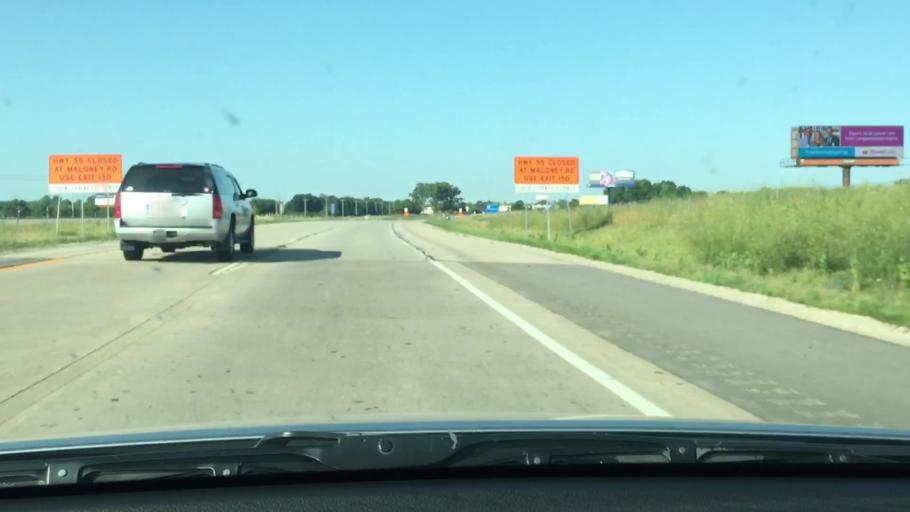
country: US
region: Wisconsin
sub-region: Outagamie County
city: Kaukauna
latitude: 44.3113
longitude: -88.2335
